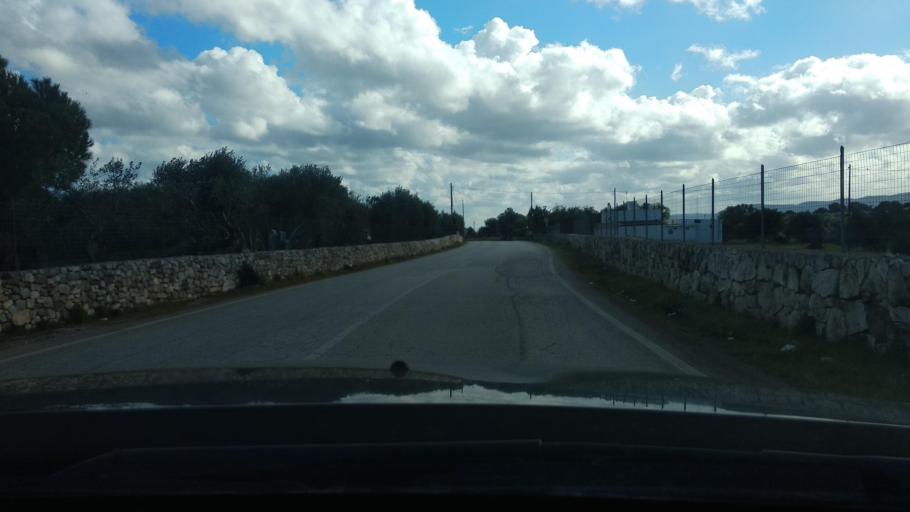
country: IT
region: Apulia
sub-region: Provincia di Brindisi
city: Pezze di Greco
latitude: 40.8252
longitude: 17.3902
